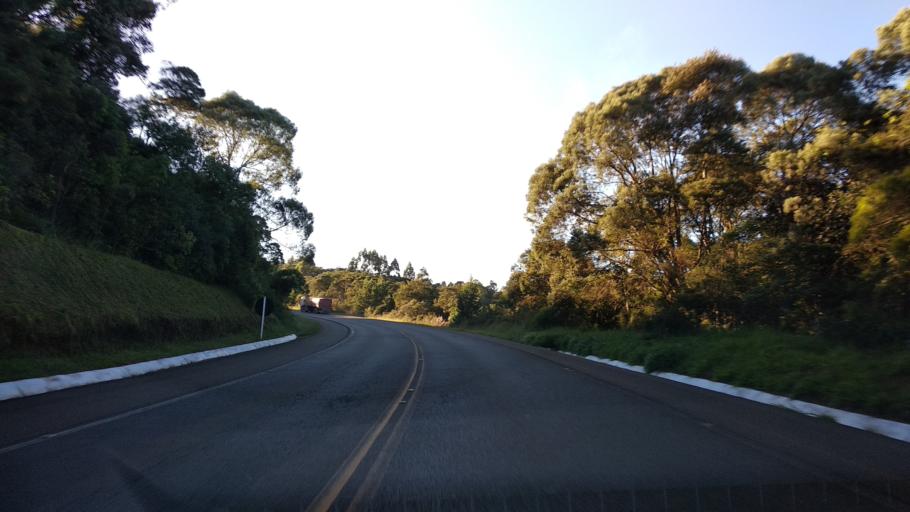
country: BR
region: Santa Catarina
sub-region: Correia Pinto
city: Correia Pinto
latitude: -27.6318
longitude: -50.6175
